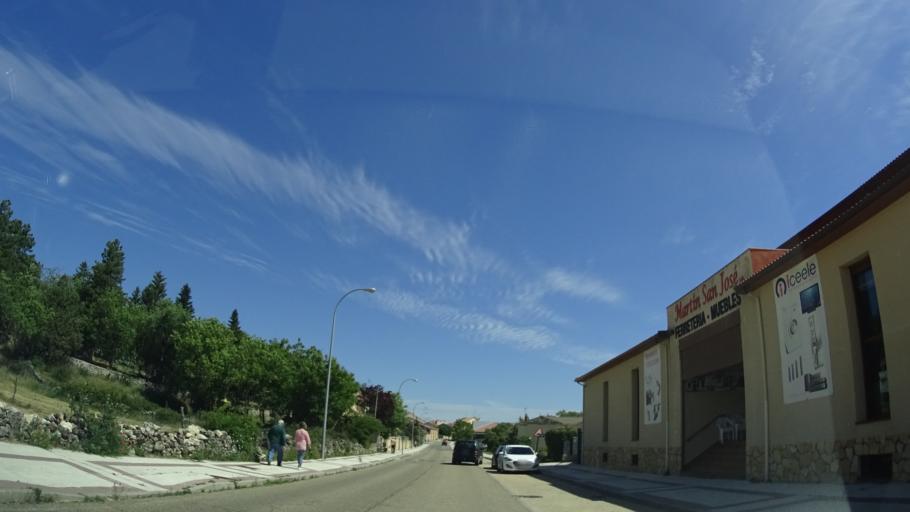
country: ES
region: Castille and Leon
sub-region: Provincia de Segovia
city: Pradena
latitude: 41.1344
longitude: -3.6886
